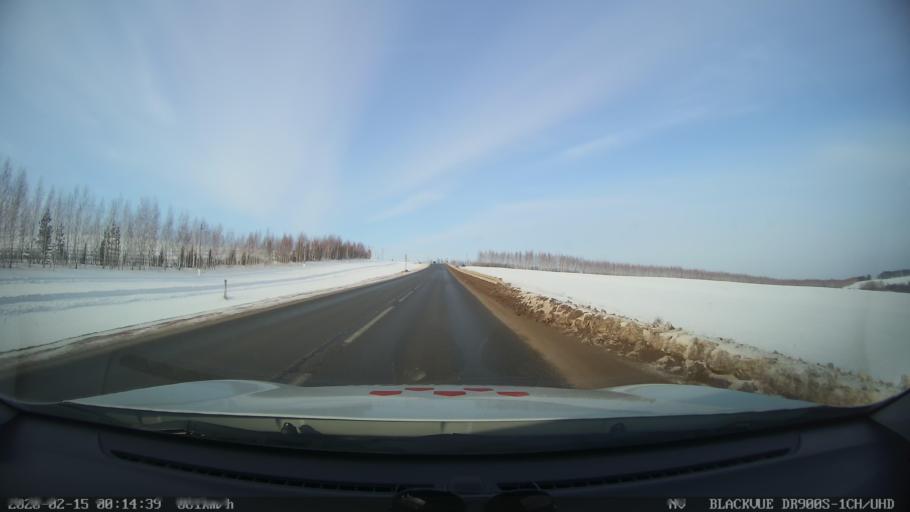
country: RU
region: Tatarstan
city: Stolbishchi
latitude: 55.4888
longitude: 49.0044
